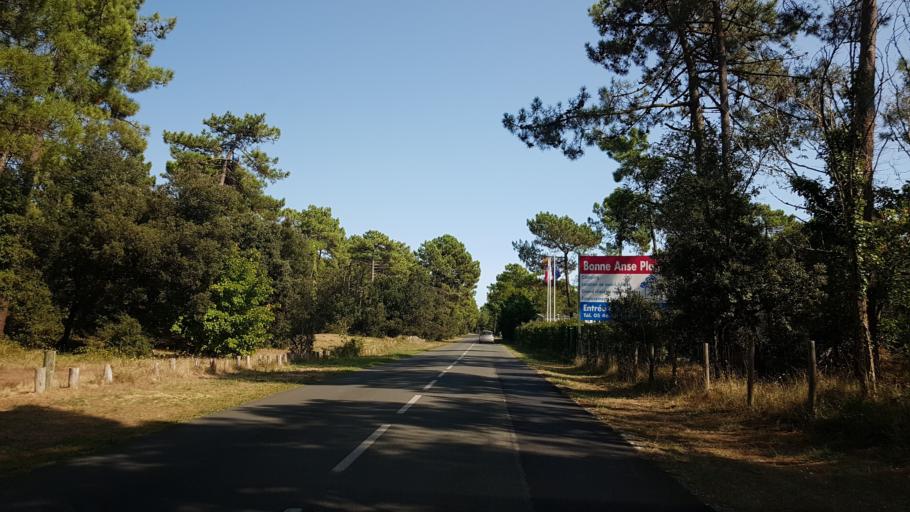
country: FR
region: Poitou-Charentes
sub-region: Departement de la Charente-Maritime
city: Les Mathes
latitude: 45.6988
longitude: -1.2027
